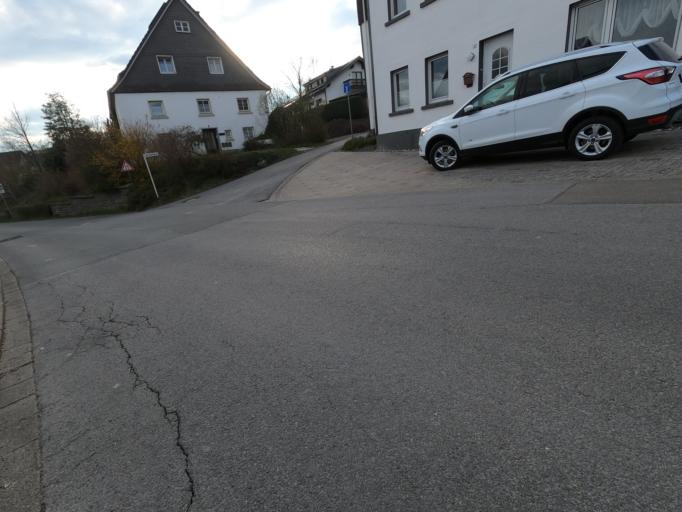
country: DE
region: North Rhine-Westphalia
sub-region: Regierungsbezirk Arnsberg
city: Herscheid
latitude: 51.1803
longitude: 7.7452
